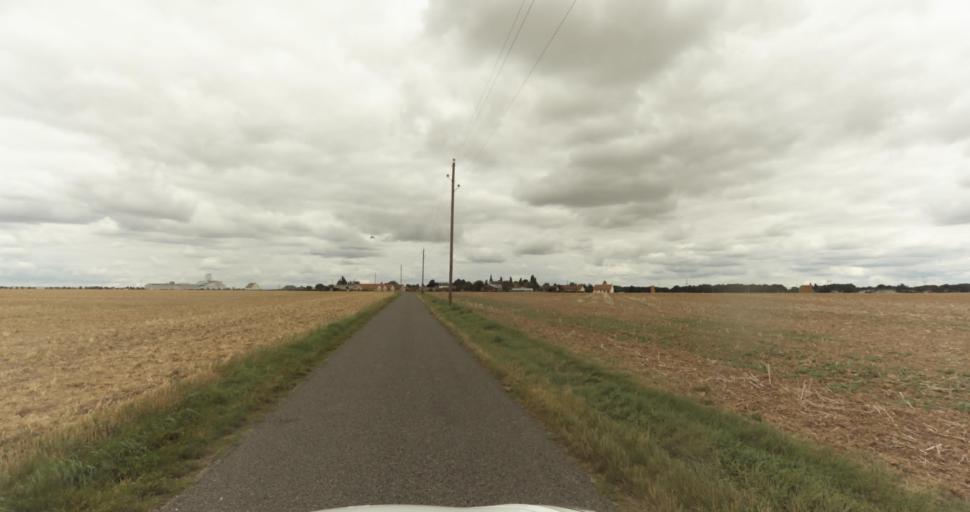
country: FR
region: Haute-Normandie
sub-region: Departement de l'Eure
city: La Madeleine-de-Nonancourt
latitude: 48.8291
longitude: 1.2030
